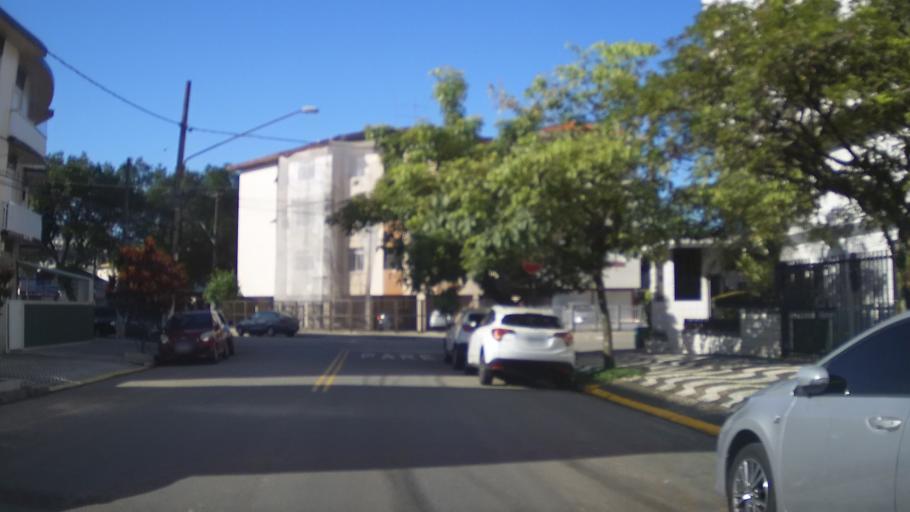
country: BR
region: Sao Paulo
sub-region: Santos
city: Santos
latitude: -23.9488
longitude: -46.3401
